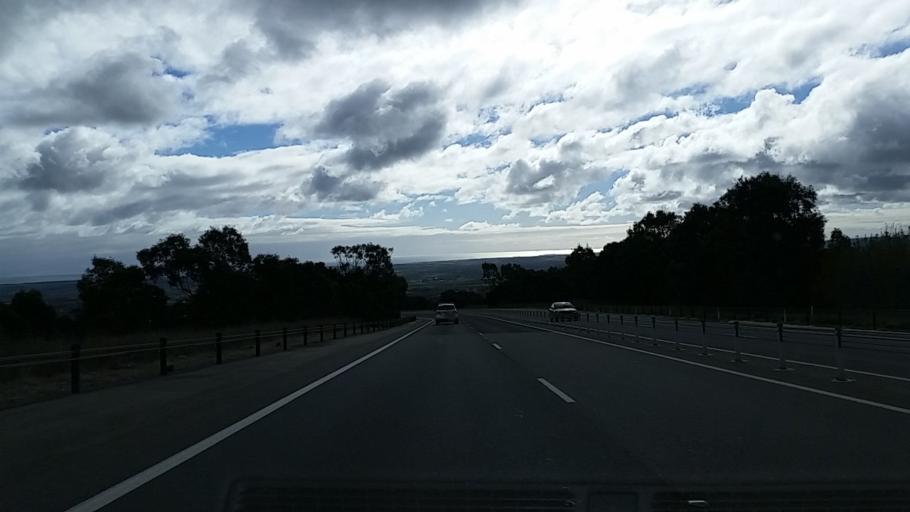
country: AU
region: South Australia
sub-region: Onkaparinga
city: McLaren Vale
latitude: -35.2846
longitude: 138.5676
